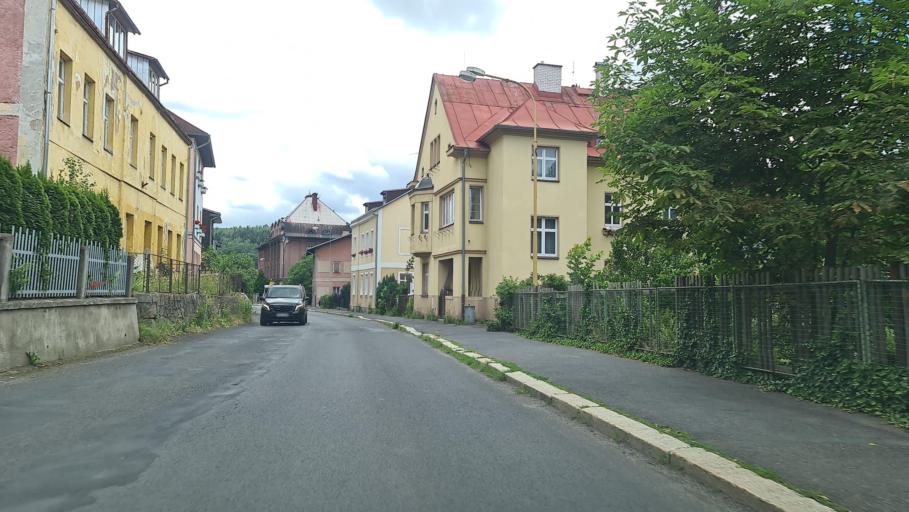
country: CZ
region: Karlovarsky
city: Kraslice
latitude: 50.3315
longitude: 12.5158
